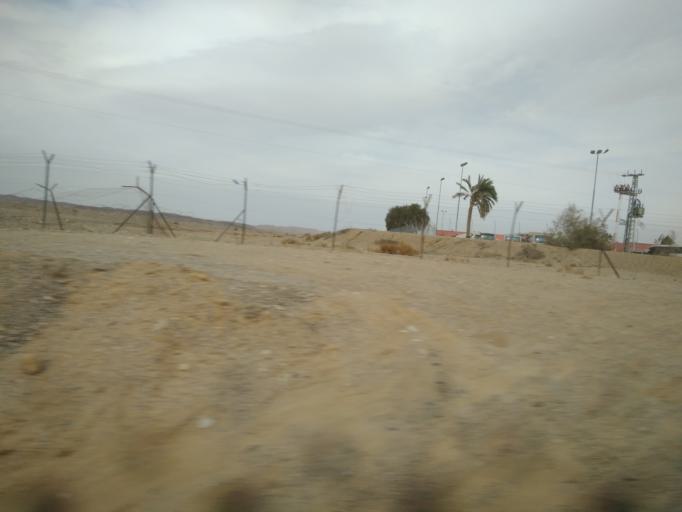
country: IL
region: Southern District
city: Eilat
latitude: 29.9515
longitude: 34.9327
